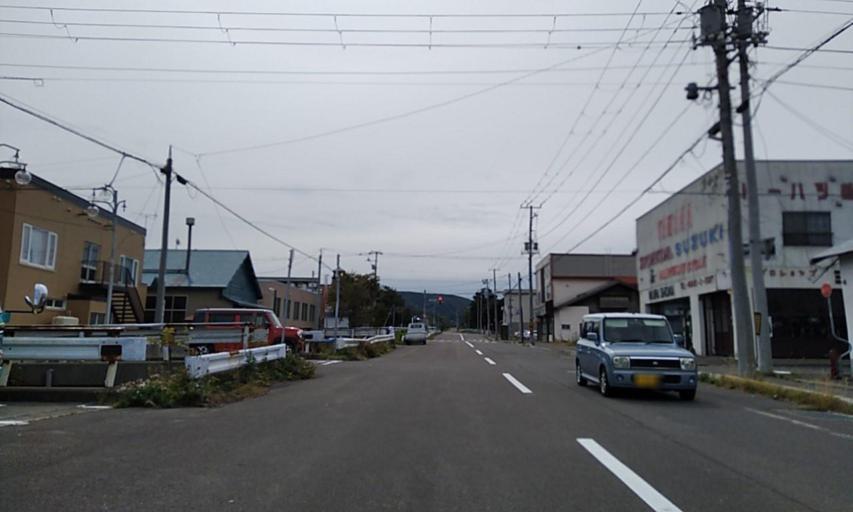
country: JP
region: Hokkaido
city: Rumoi
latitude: 43.8568
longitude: 141.5217
